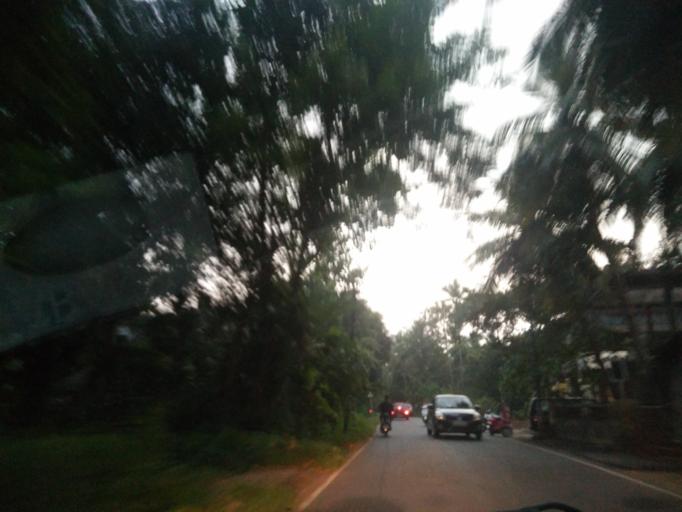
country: IN
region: Goa
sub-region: South Goa
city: Chinchinim
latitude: 15.2241
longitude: 73.9995
